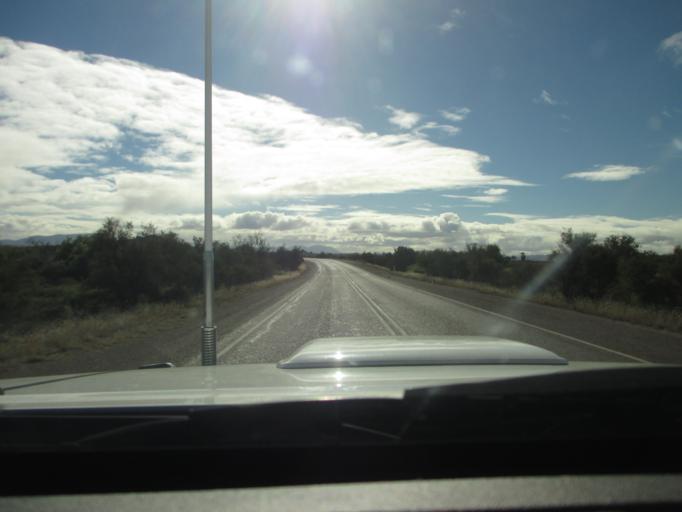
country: AU
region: South Australia
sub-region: Flinders Ranges
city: Quorn
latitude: -31.9070
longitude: 138.4347
